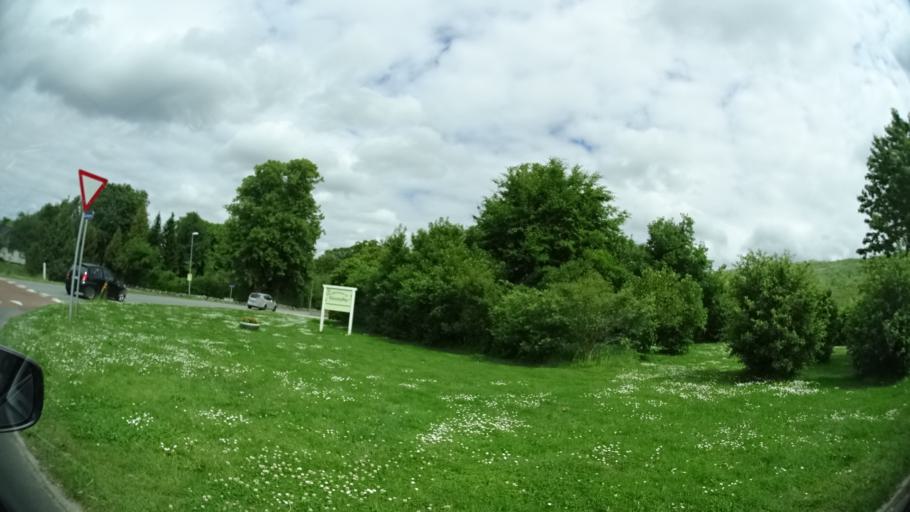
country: DK
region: Central Jutland
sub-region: Syddjurs Kommune
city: Ryomgard
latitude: 56.4052
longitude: 10.5639
